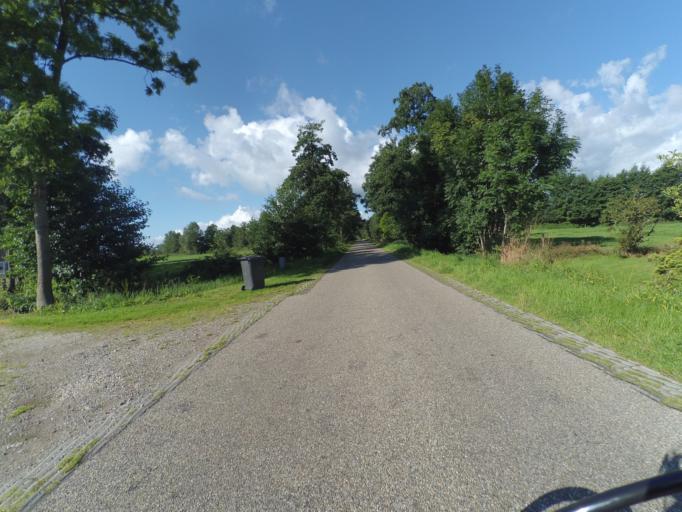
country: NL
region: Friesland
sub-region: Gemeente Kollumerland en Nieuwkruisland
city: Kollumerzwaag
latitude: 53.2783
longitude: 6.0840
